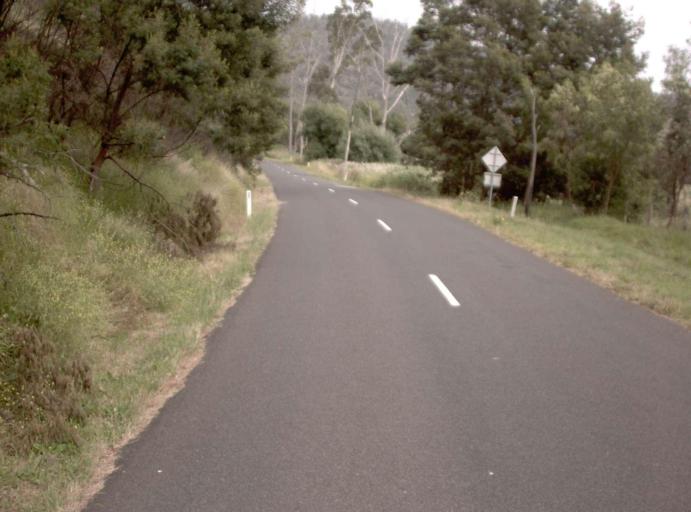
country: AU
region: Victoria
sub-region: Wellington
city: Heyfield
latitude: -37.7902
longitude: 146.6780
